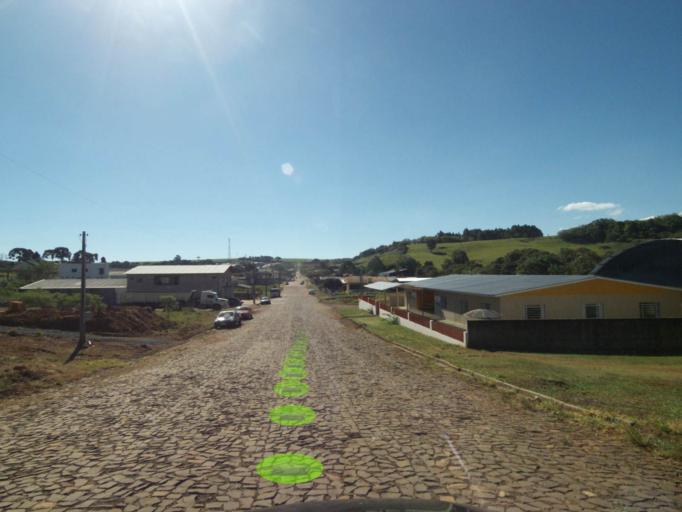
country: BR
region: Parana
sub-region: Coronel Vivida
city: Coronel Vivida
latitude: -26.1432
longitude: -52.3791
